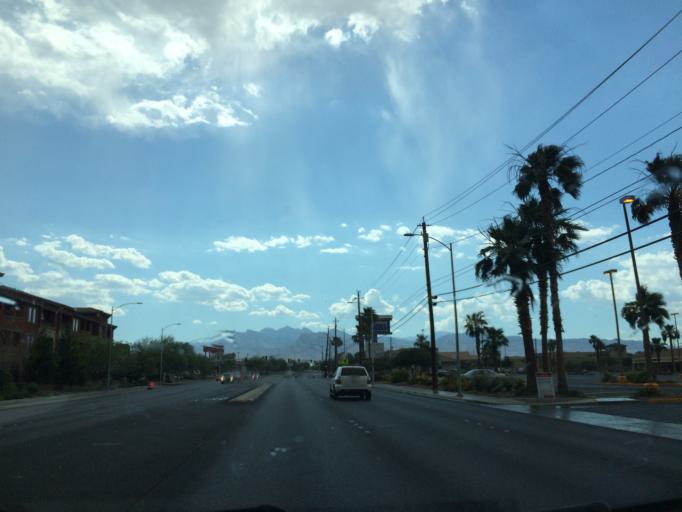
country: US
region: Nevada
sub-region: Clark County
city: Las Vegas
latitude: 36.2169
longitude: -115.2232
